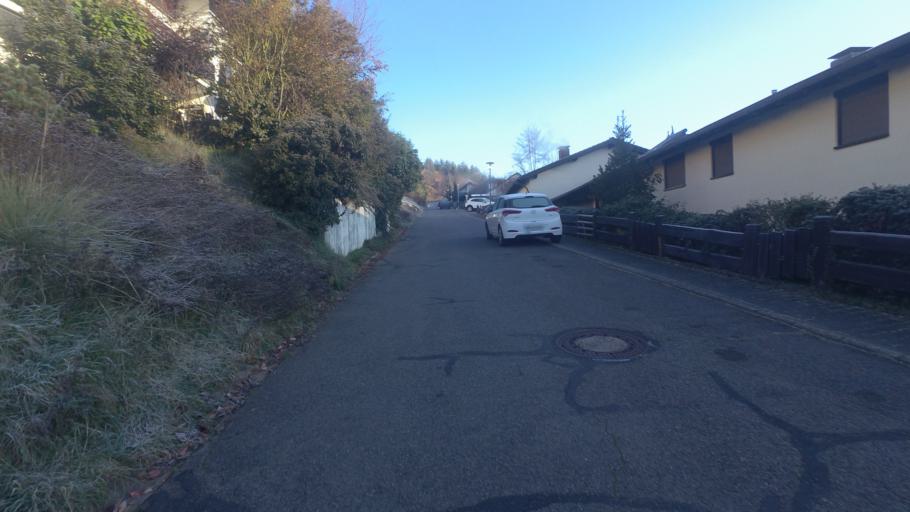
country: DE
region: Baden-Wuerttemberg
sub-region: Karlsruhe Region
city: Heiligkreuzsteinach
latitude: 49.4880
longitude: 8.7996
